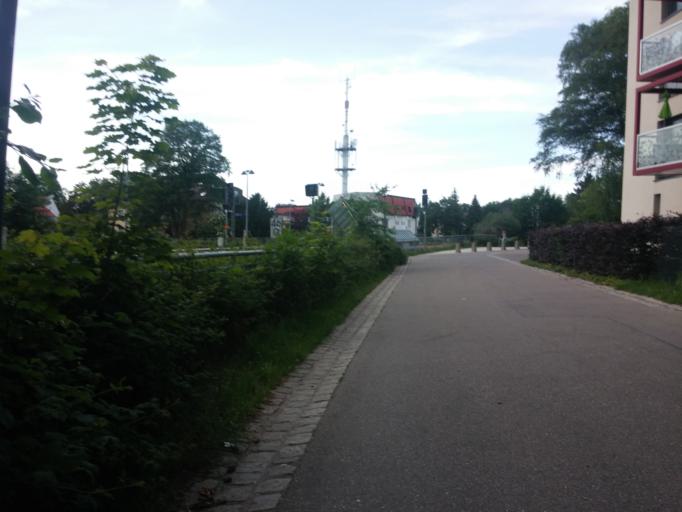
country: DE
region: Bavaria
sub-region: Swabia
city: Memmingen
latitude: 47.9864
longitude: 10.1874
